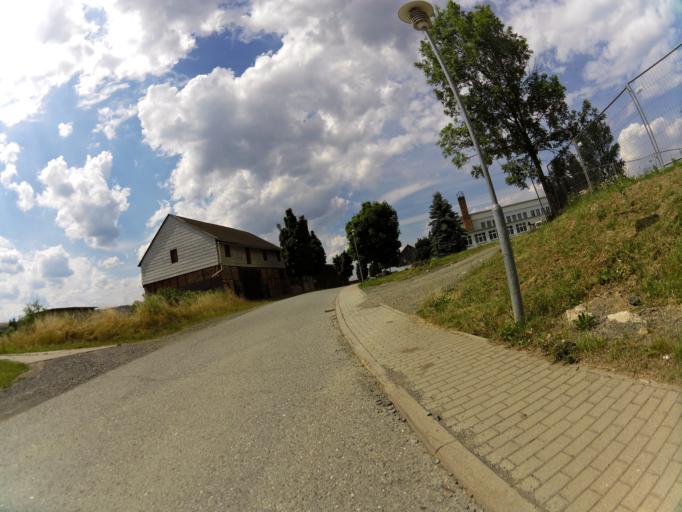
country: DE
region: Thuringia
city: Burgk
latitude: 50.5043
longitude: 11.7295
